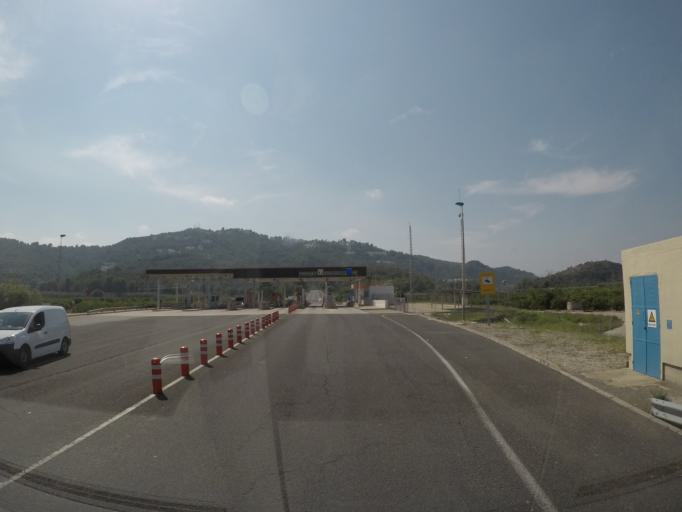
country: ES
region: Valencia
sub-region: Provincia de Valencia
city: L'Alqueria de la Comtessa
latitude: 38.9266
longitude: -0.1369
